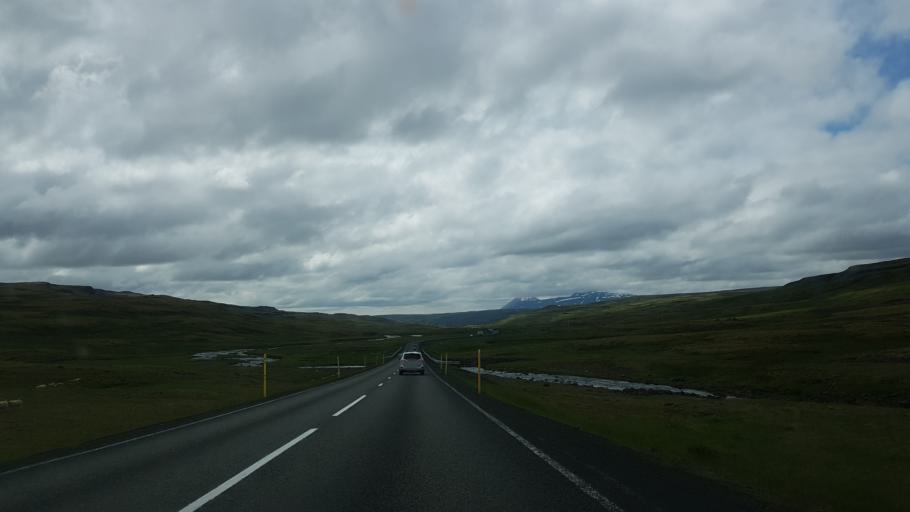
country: IS
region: West
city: Borgarnes
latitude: 64.9352
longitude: -21.0705
